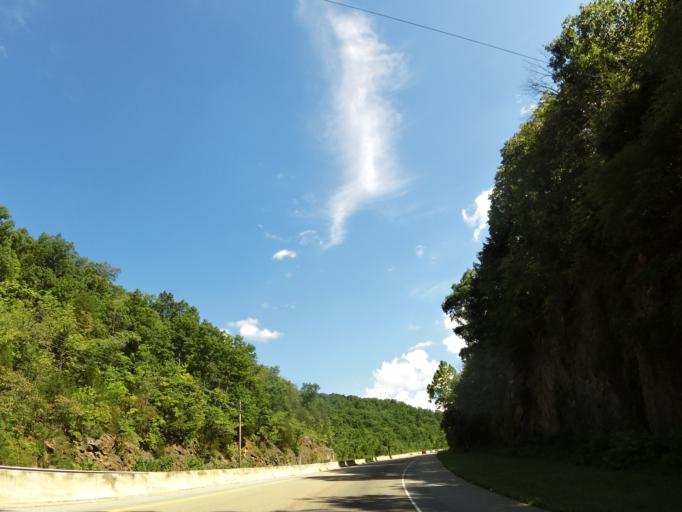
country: US
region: Tennessee
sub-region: Grainger County
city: Rutledge
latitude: 36.3753
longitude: -83.4414
